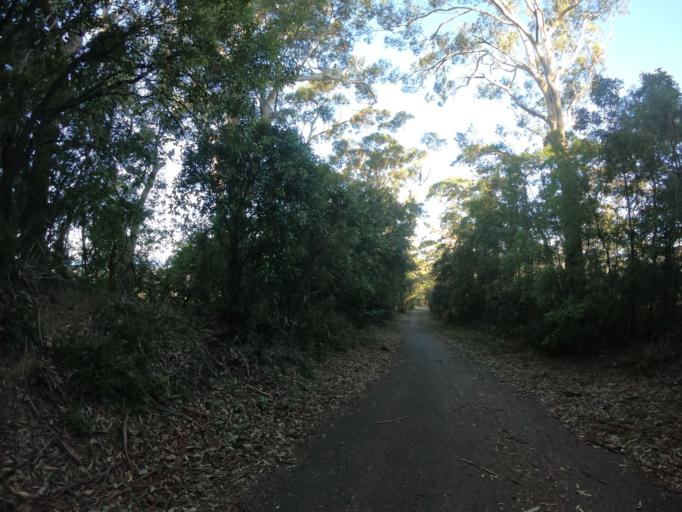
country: AU
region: New South Wales
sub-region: Wollongong
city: Mount Keira
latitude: -34.4118
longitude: 150.8355
